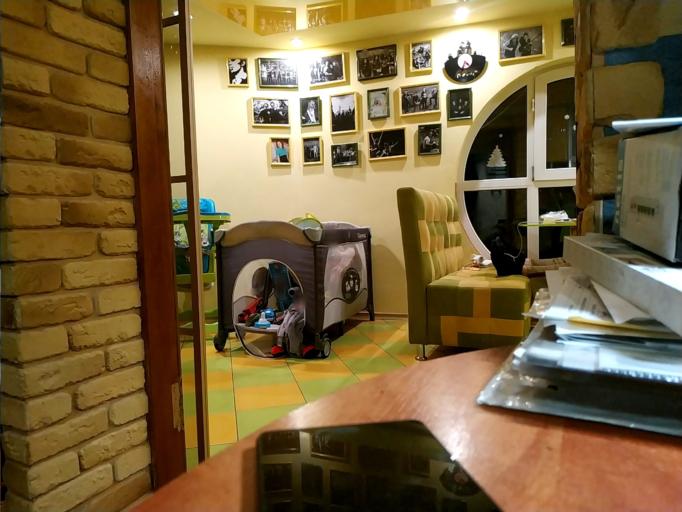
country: RU
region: Orjol
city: Naryshkino
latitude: 53.0396
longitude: 35.6822
